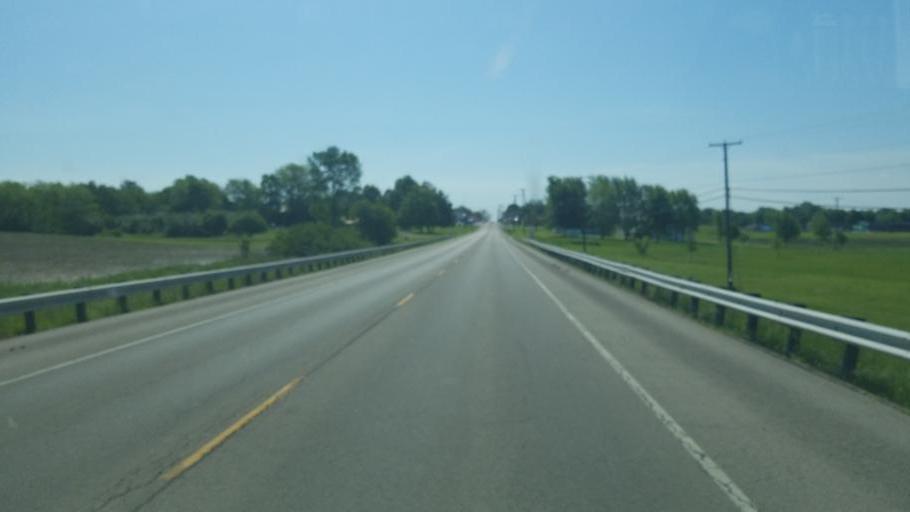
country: US
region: Ohio
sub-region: Hardin County
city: Kenton
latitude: 40.6533
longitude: -83.6283
